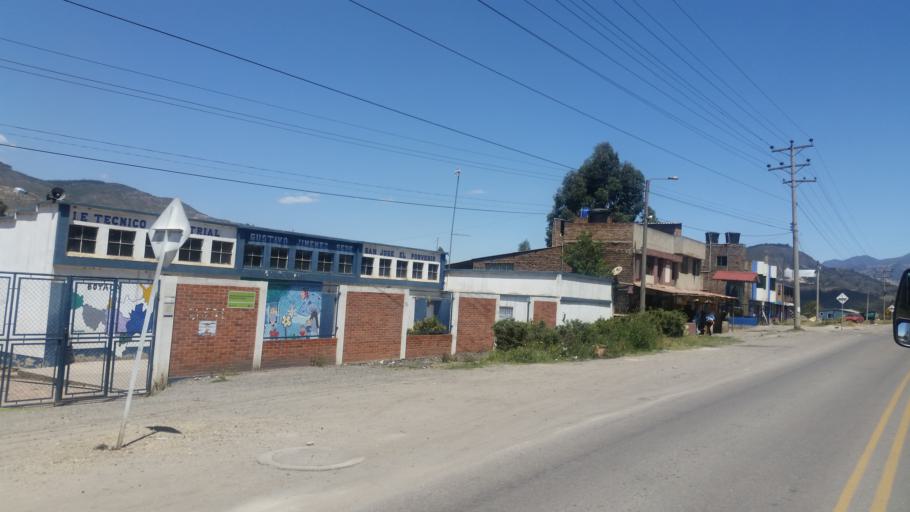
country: CO
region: Boyaca
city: Mongui
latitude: 5.7615
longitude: -72.8844
